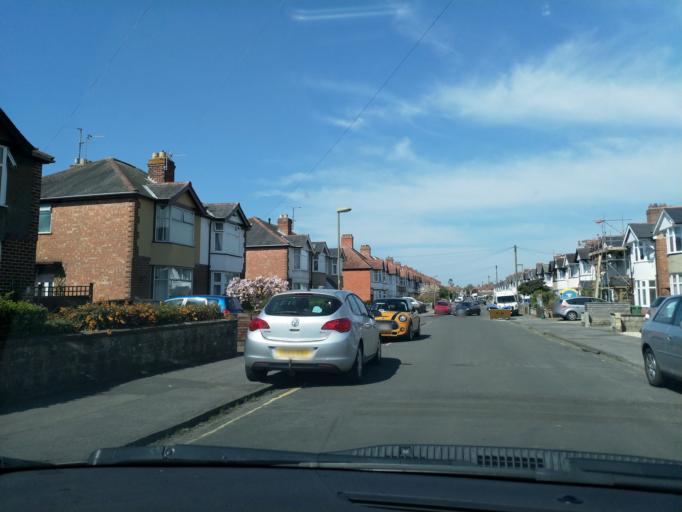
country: GB
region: England
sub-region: Oxfordshire
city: Cowley
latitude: 51.7345
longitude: -1.2005
